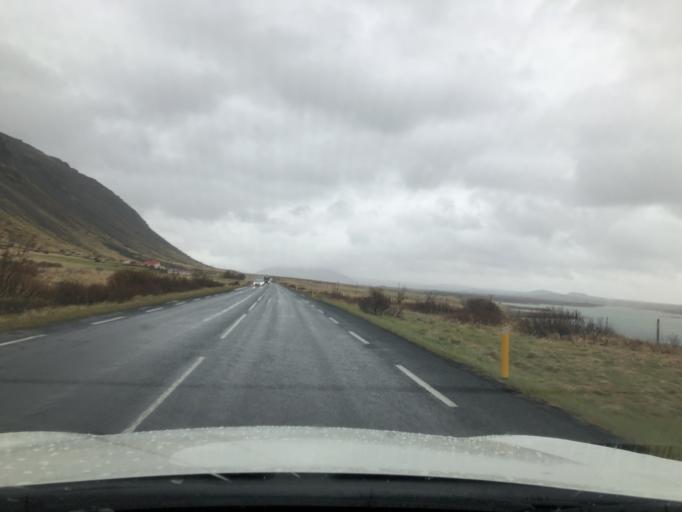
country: IS
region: South
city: Selfoss
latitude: 63.9756
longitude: -20.9853
